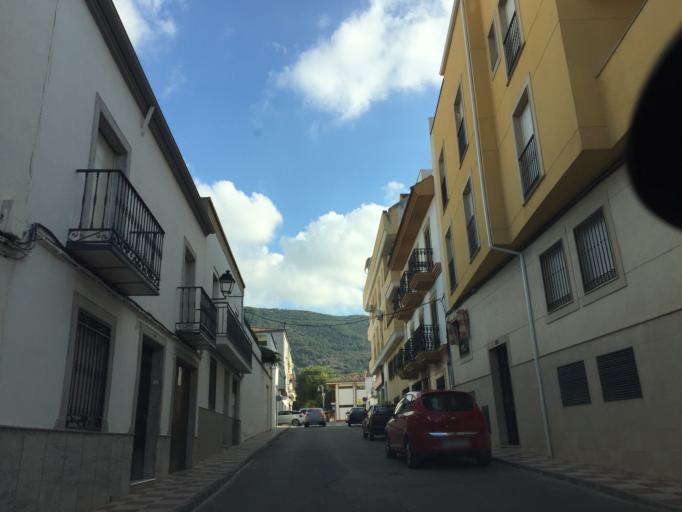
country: ES
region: Andalusia
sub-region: Provincia de Jaen
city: Mancha Real
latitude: 37.7838
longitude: -3.6095
